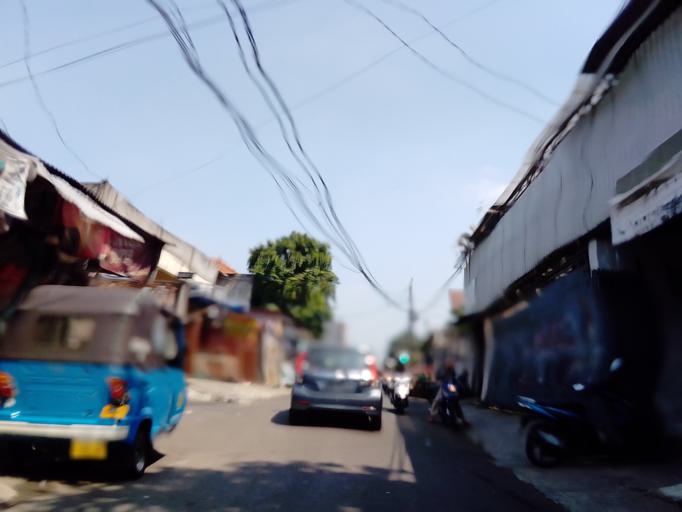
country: ID
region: Jakarta Raya
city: Jakarta
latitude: -6.2599
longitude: 106.8040
